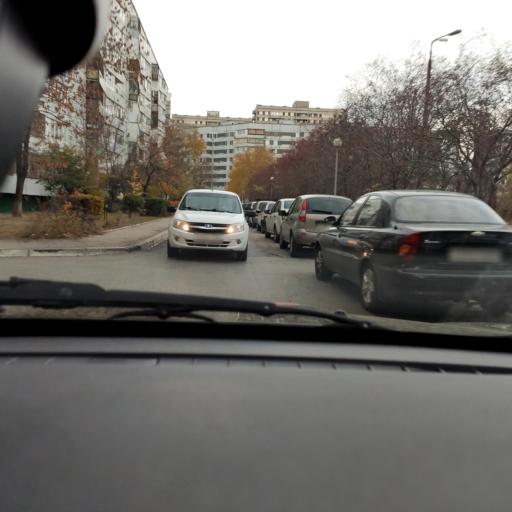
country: RU
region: Samara
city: Tol'yatti
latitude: 53.5237
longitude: 49.3173
